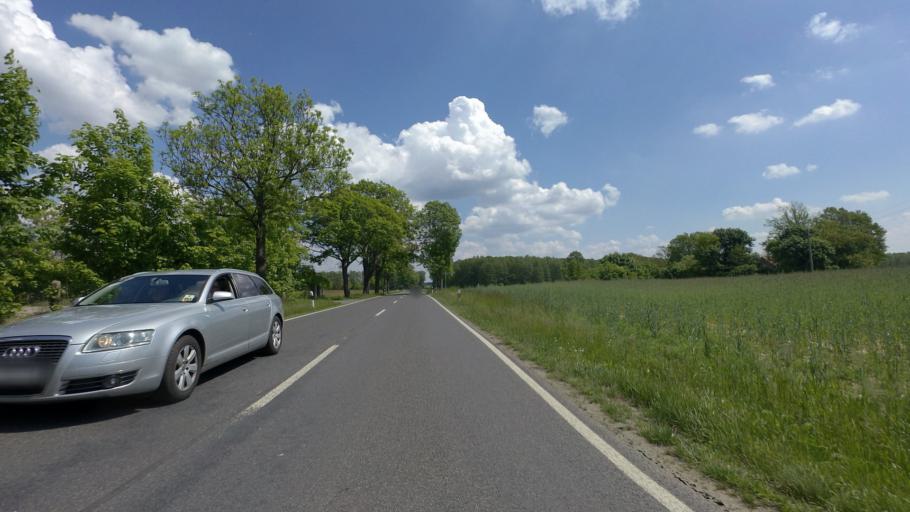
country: DE
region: Brandenburg
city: Straupitz
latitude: 51.9143
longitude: 14.1323
